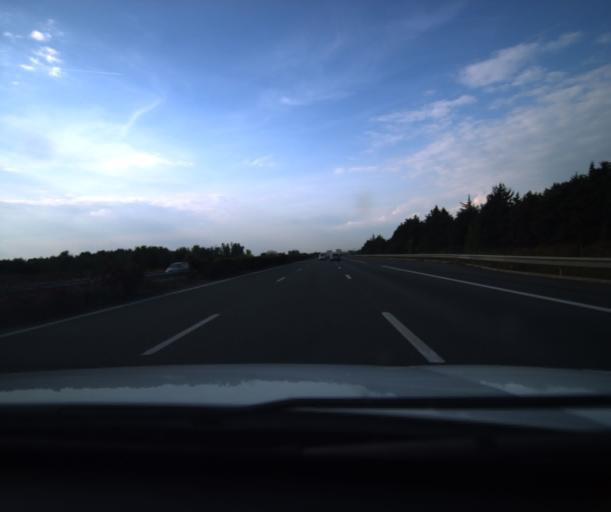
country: FR
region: Midi-Pyrenees
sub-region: Departement du Tarn-et-Garonne
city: Campsas
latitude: 43.8787
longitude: 1.3169
